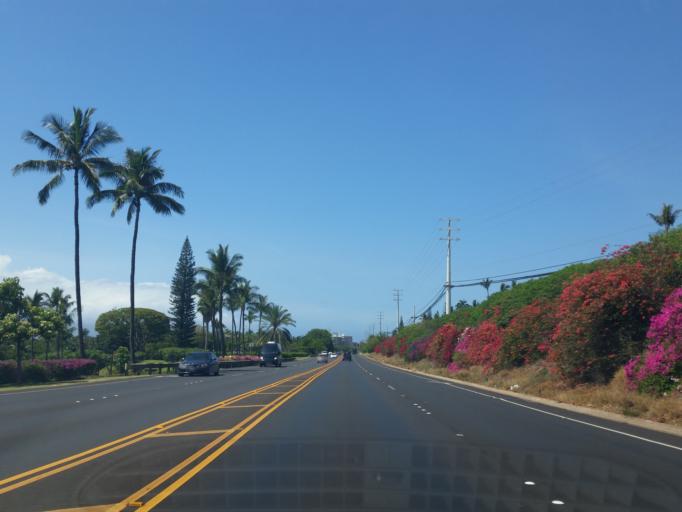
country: US
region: Hawaii
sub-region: Maui County
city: Kaanapali Landing
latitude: 20.9293
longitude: -156.6900
